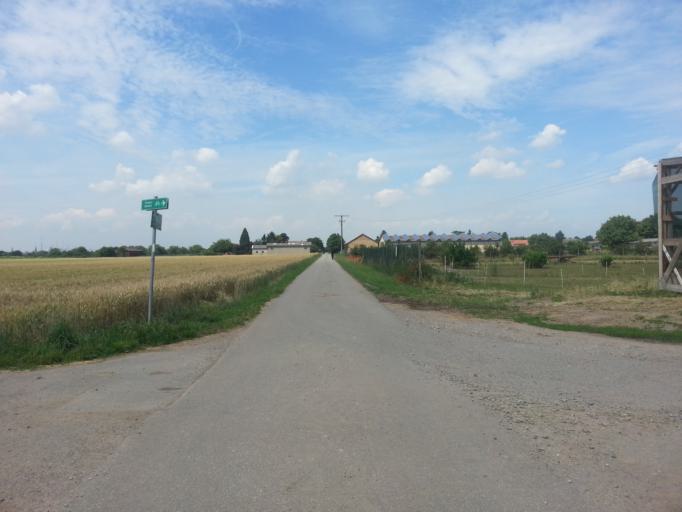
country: DE
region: Baden-Wuerttemberg
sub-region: Karlsruhe Region
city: Edingen-Neckarhausen
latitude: 49.4380
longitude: 8.6105
